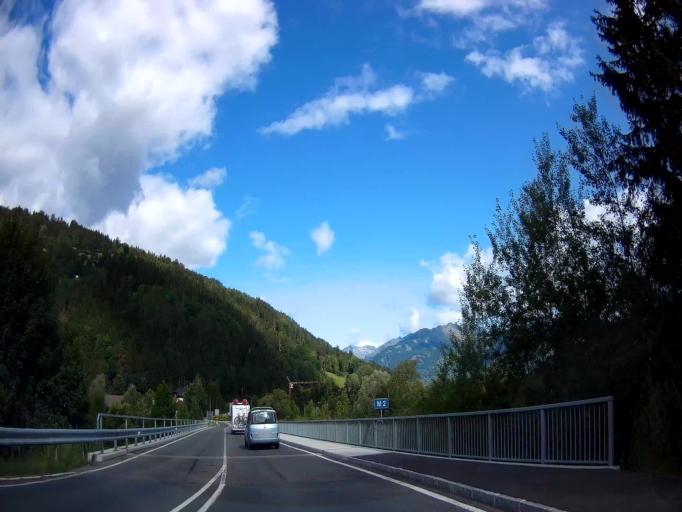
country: AT
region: Carinthia
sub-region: Politischer Bezirk Spittal an der Drau
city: Gmuend
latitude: 46.9022
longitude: 13.5332
